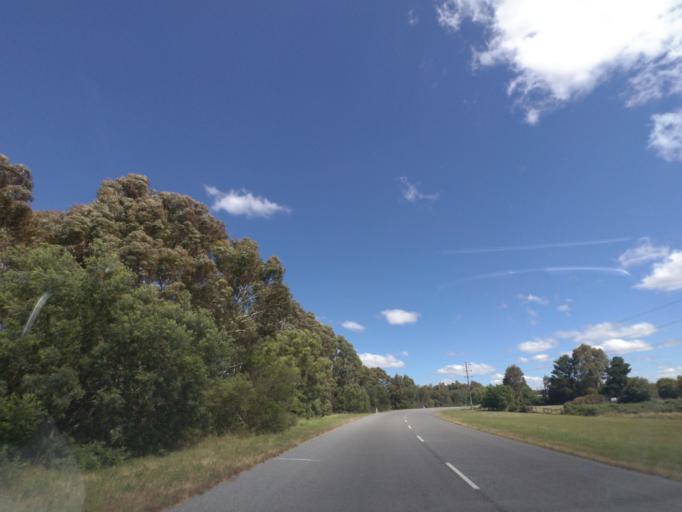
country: AU
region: Victoria
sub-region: Hume
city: Sunbury
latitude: -37.3203
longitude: 144.5237
